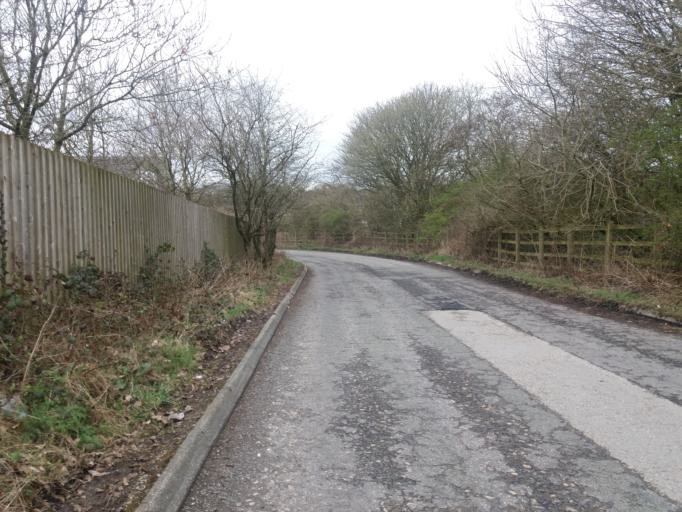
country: GB
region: England
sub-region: Lancashire
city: Chorley
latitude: 53.6558
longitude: -2.6114
